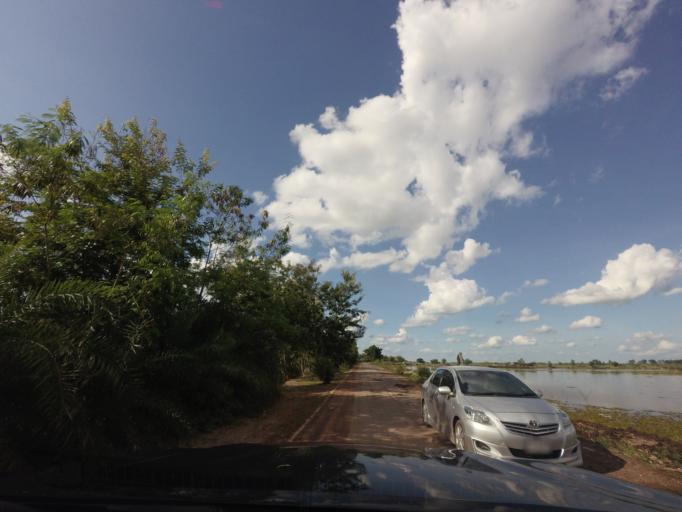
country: TH
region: Changwat Udon Thani
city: Ban Dung
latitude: 17.7464
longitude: 103.3572
